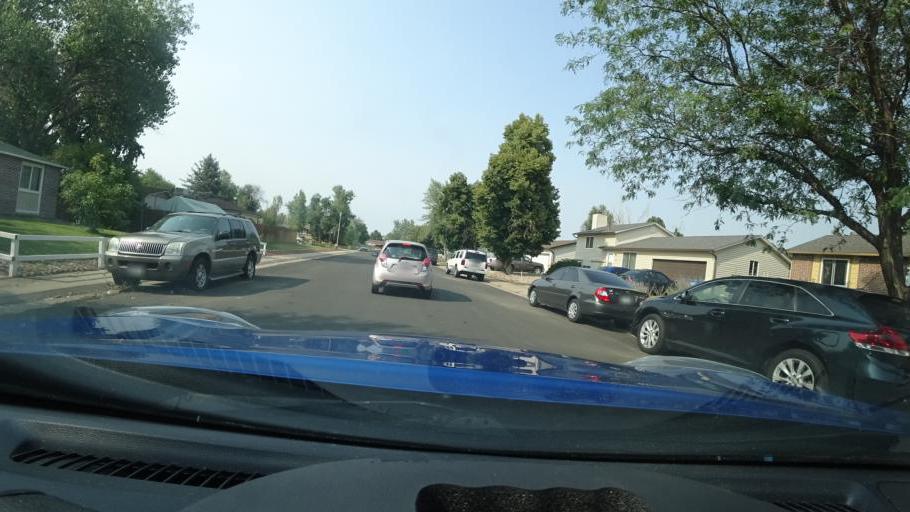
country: US
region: Colorado
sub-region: Adams County
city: Aurora
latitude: 39.6647
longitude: -104.8069
